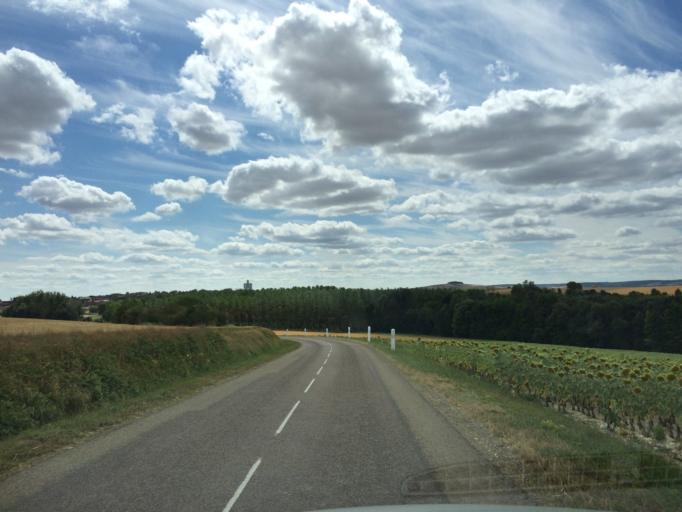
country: FR
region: Bourgogne
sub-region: Departement de l'Yonne
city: Laroche-Saint-Cydroine
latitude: 47.9297
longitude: 3.4456
